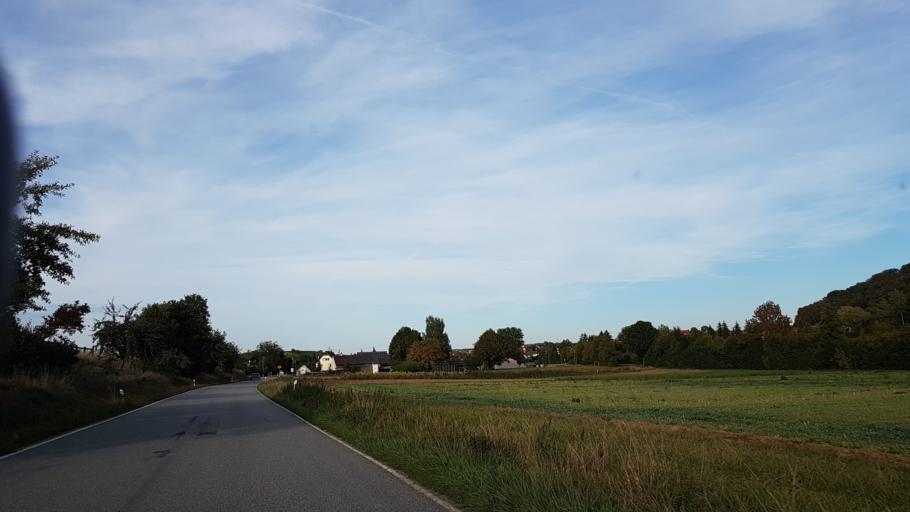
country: DE
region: Baden-Wuerttemberg
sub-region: Regierungsbezirk Stuttgart
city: Neuenstadt am Kocher
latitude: 49.2095
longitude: 9.3487
